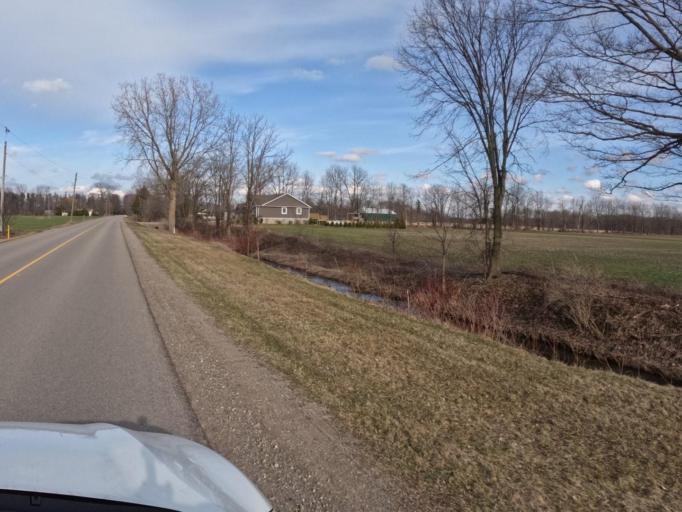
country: CA
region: Ontario
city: Brant
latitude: 43.0012
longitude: -80.4396
